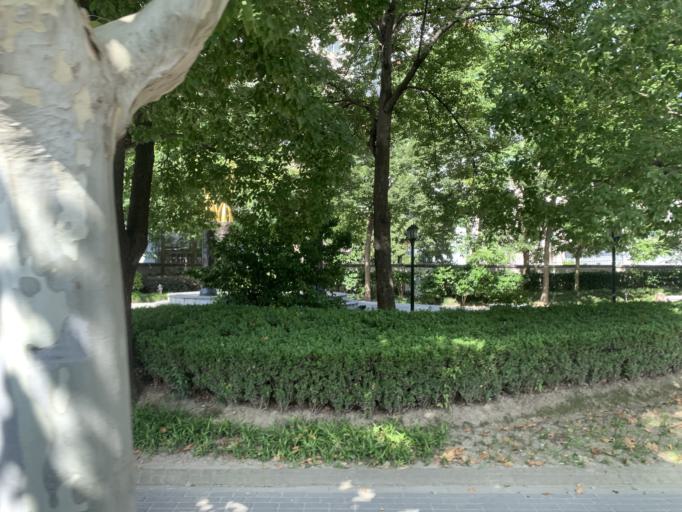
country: CN
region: Shanghai Shi
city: Pudong
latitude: 31.2346
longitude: 121.5195
